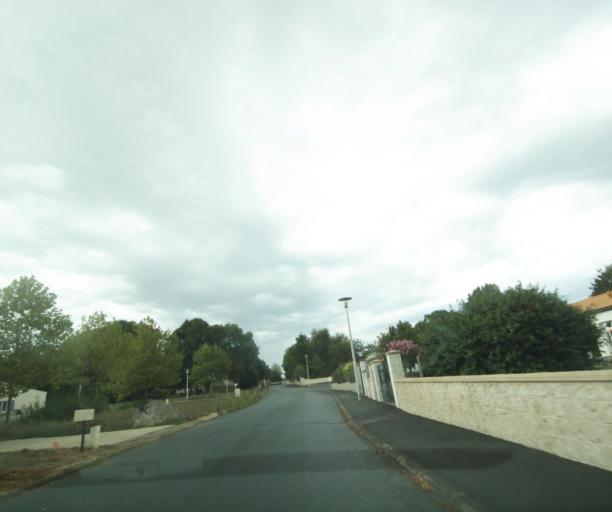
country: FR
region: Poitou-Charentes
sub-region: Departement de la Charente-Maritime
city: Tonnay-Charente
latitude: 45.9450
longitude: -0.8794
